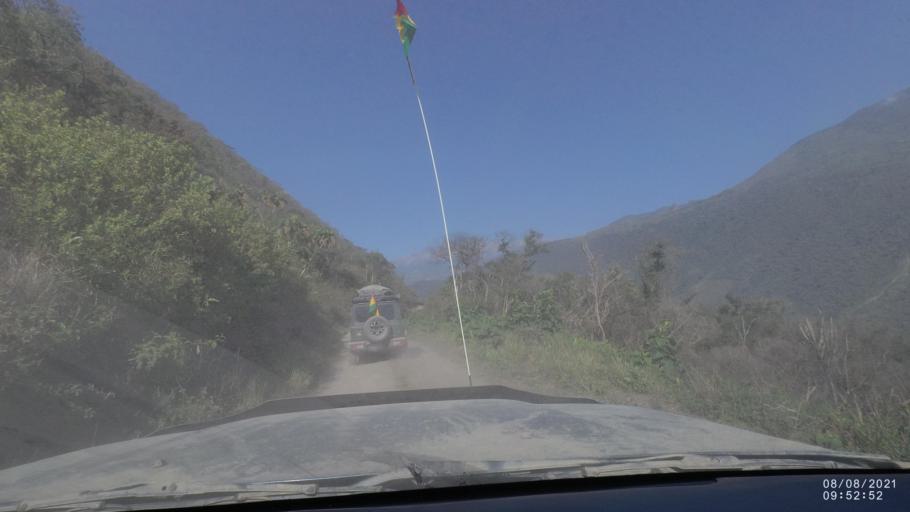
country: BO
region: La Paz
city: Quime
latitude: -16.6262
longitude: -66.7314
